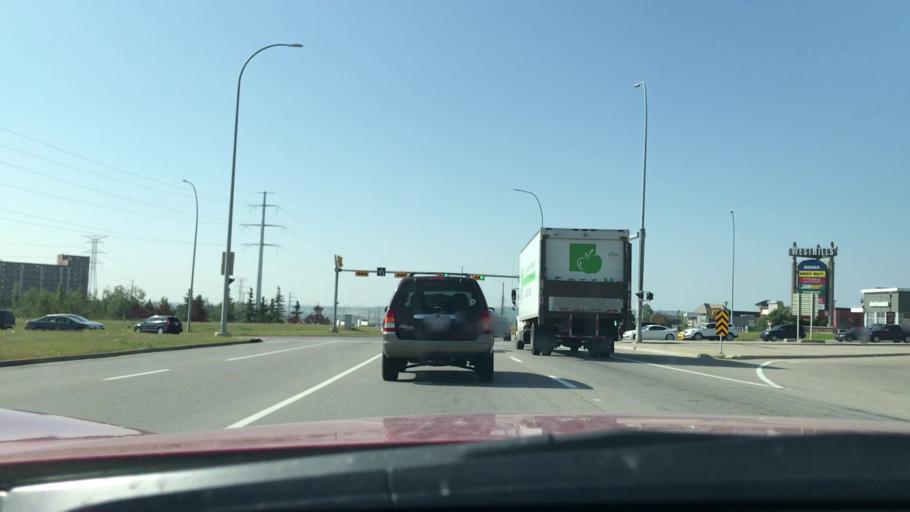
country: CA
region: Alberta
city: Calgary
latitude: 51.0186
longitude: -114.1661
